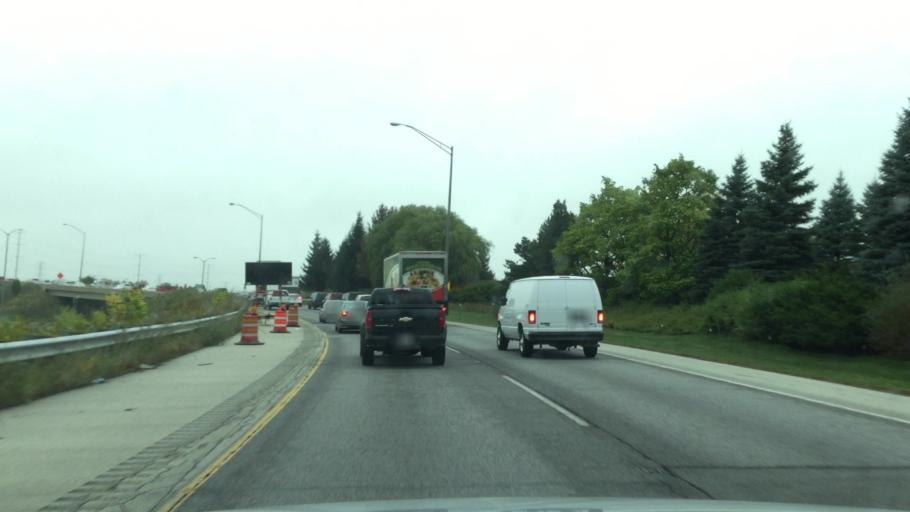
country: US
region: Illinois
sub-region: Cook County
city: Glencoe
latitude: 42.1448
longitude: -87.7923
